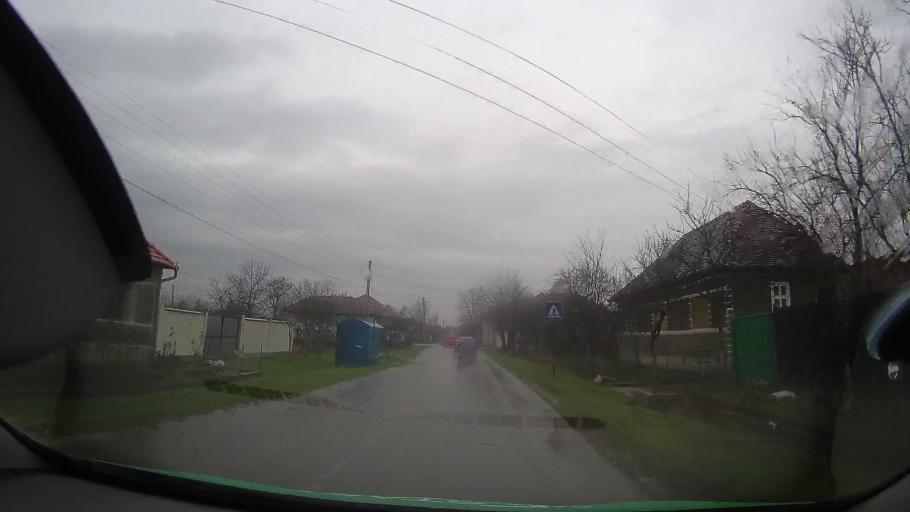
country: RO
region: Bihor
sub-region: Comuna Holod
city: Vintere
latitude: 46.7448
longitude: 22.1391
